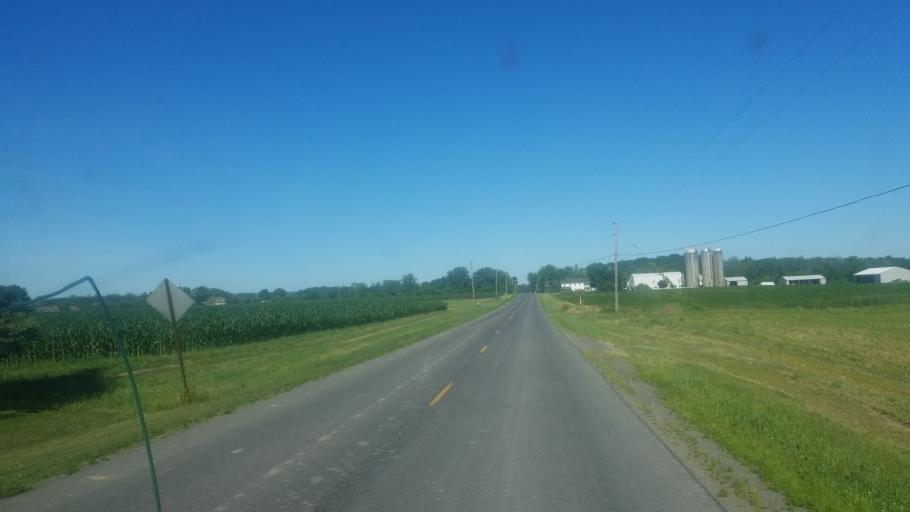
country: US
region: New York
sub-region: Ontario County
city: Canandaigua
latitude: 42.8359
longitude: -77.2026
